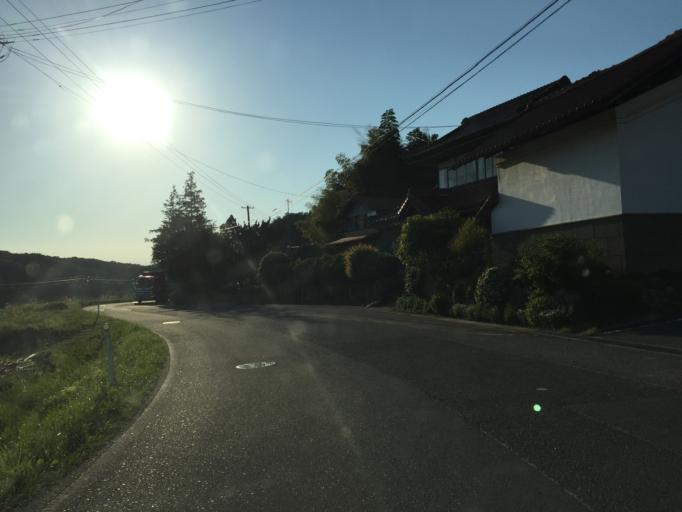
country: JP
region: Fukushima
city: Ishikawa
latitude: 37.0441
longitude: 140.4339
